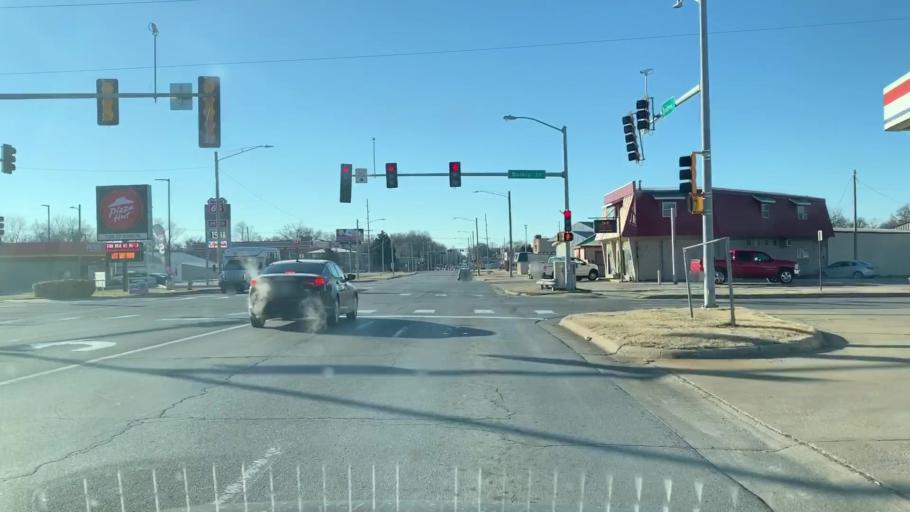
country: US
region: Kansas
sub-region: Crawford County
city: Pittsburg
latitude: 37.3967
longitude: -94.7051
